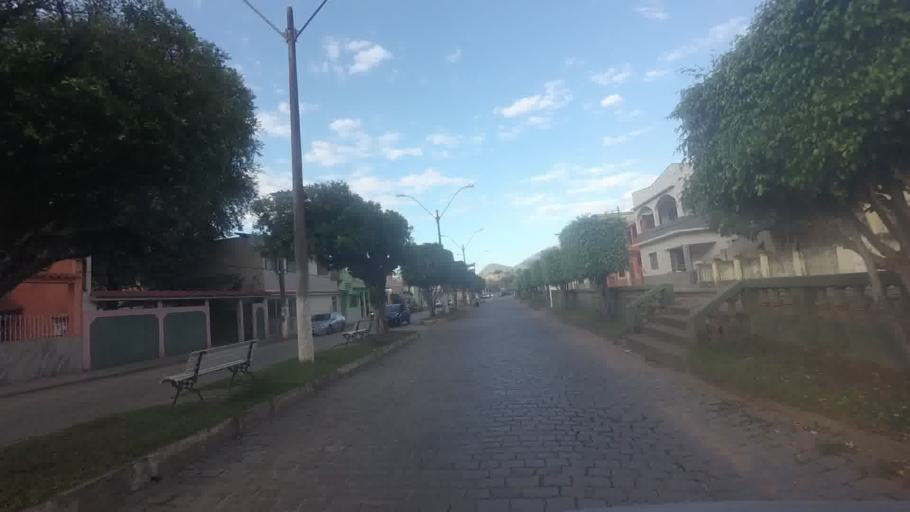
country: BR
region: Espirito Santo
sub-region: Mimoso Do Sul
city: Mimoso do Sul
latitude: -20.9485
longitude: -41.3410
